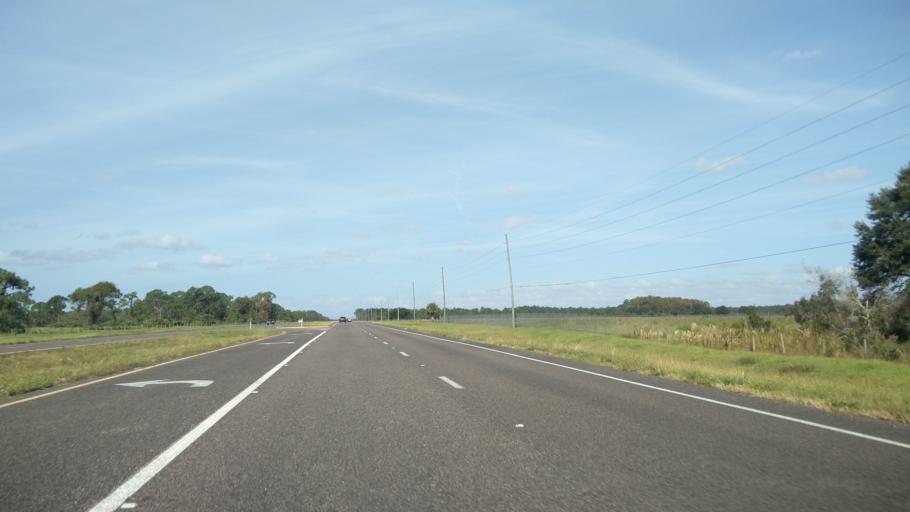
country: US
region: Florida
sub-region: Brevard County
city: June Park
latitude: 28.1044
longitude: -80.9042
